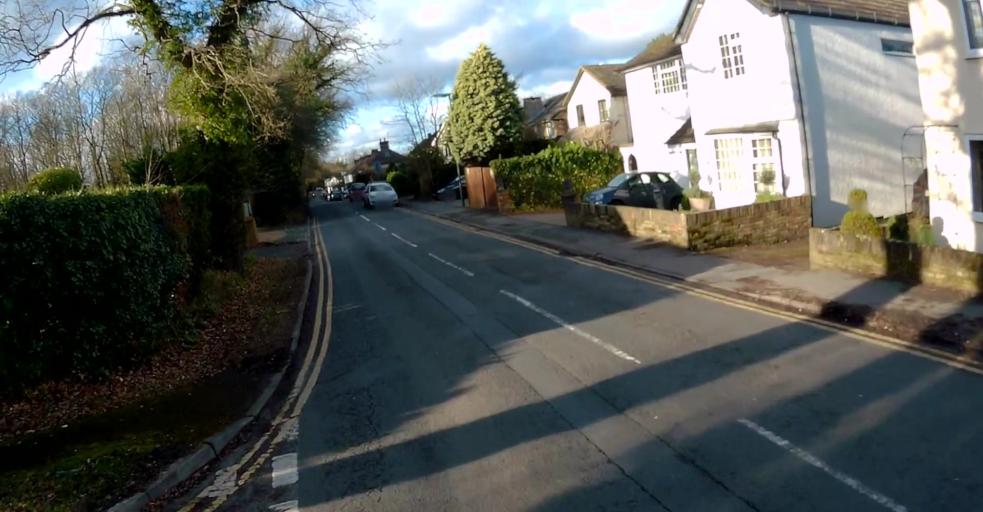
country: GB
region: England
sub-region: Surrey
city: Ottershaw
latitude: 51.3648
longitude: -0.5149
